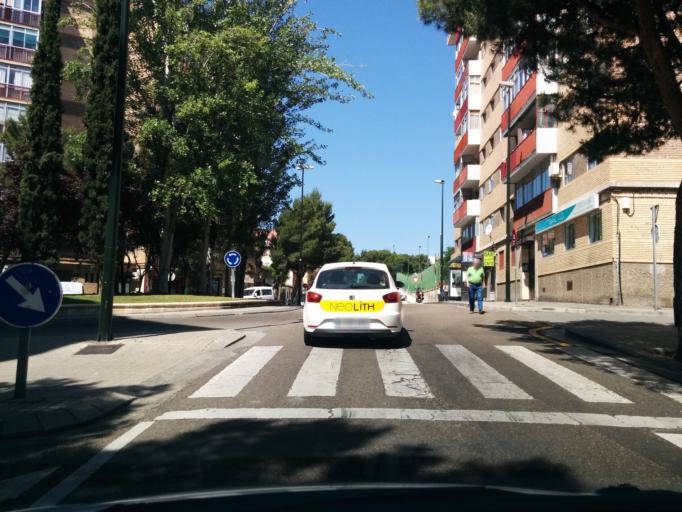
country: ES
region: Aragon
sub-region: Provincia de Zaragoza
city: Zaragoza
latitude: 41.6248
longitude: -0.8760
